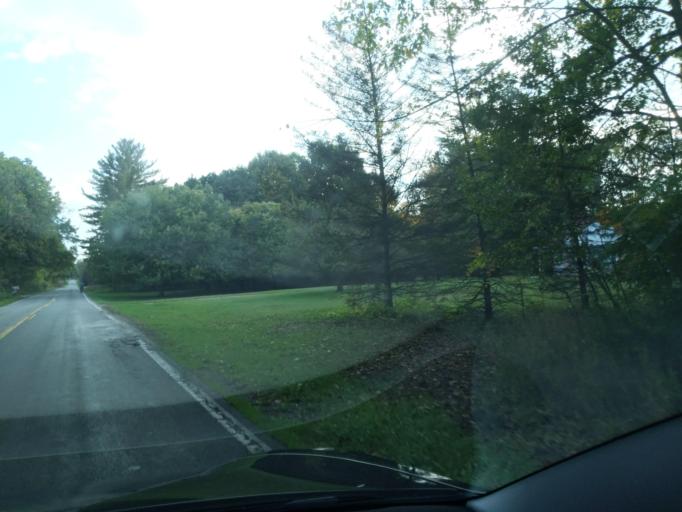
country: US
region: Michigan
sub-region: Jackson County
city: Jackson
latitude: 42.2873
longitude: -84.4831
